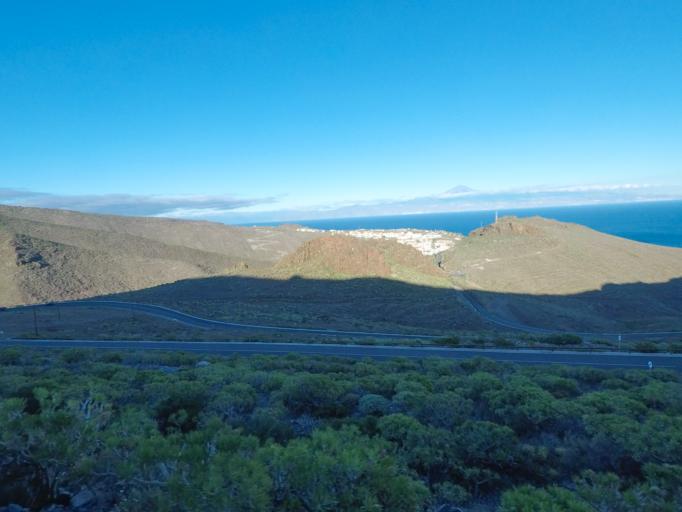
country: ES
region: Canary Islands
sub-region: Provincia de Santa Cruz de Tenerife
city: San Sebastian de la Gomera
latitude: 28.0824
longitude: -17.1295
